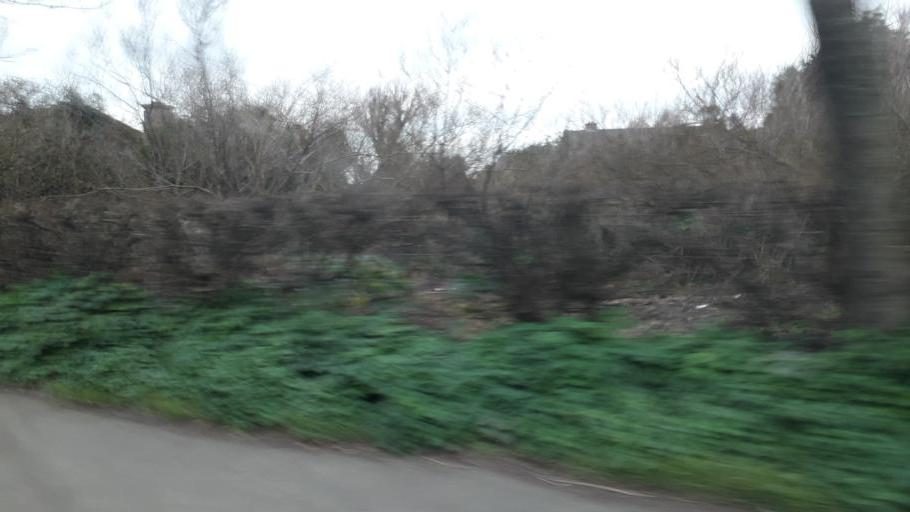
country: IE
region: Leinster
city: An Ros
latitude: 53.5205
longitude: -6.1116
